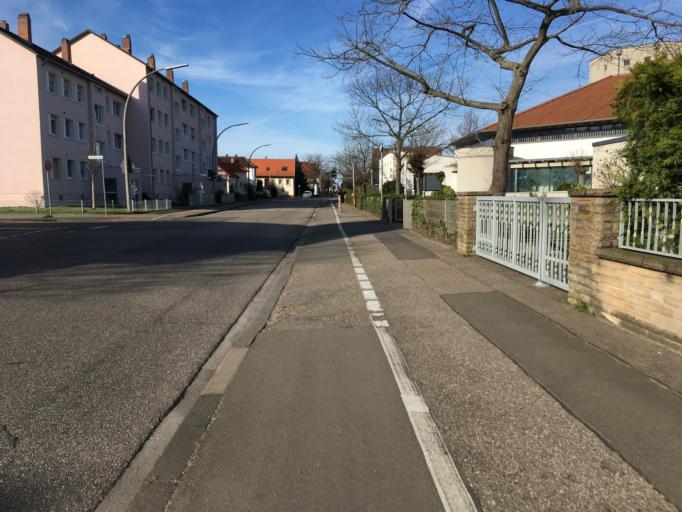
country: DE
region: Rheinland-Pfalz
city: Neustadt
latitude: 49.3478
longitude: 8.1636
